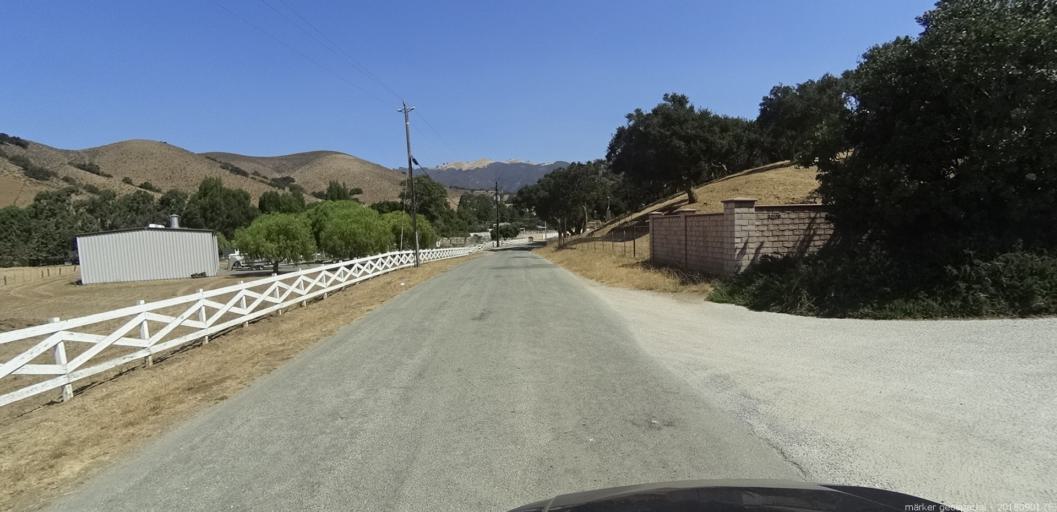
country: US
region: California
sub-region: Monterey County
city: Chualar
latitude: 36.5987
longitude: -121.4351
